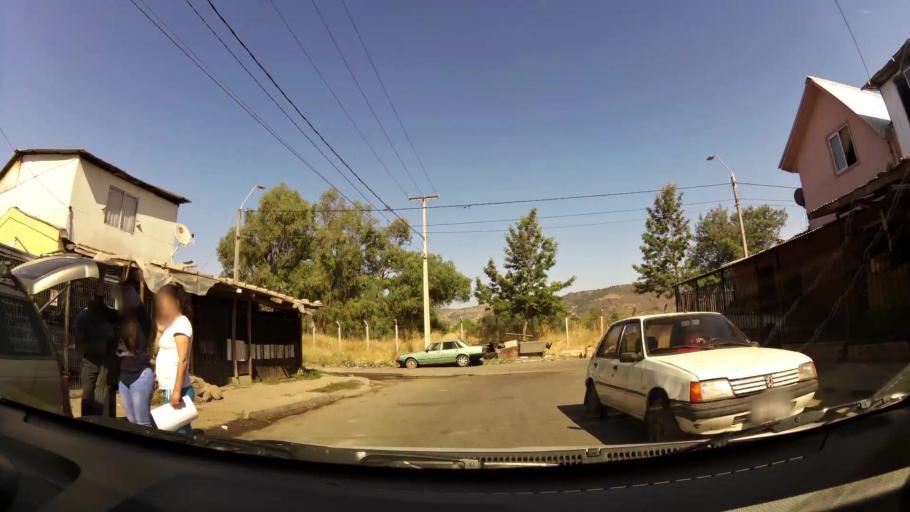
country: CL
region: Maule
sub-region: Provincia de Talca
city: Talca
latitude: -35.3958
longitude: -71.6541
